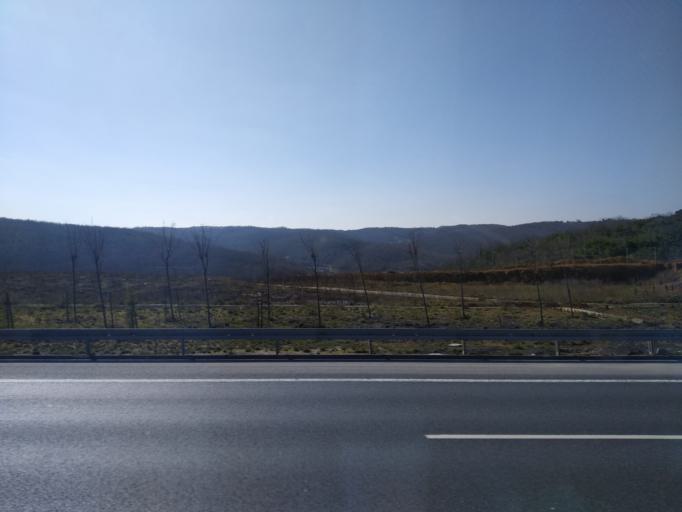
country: TR
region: Istanbul
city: Mahmut Sevket Pasa
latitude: 41.1780
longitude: 29.2383
